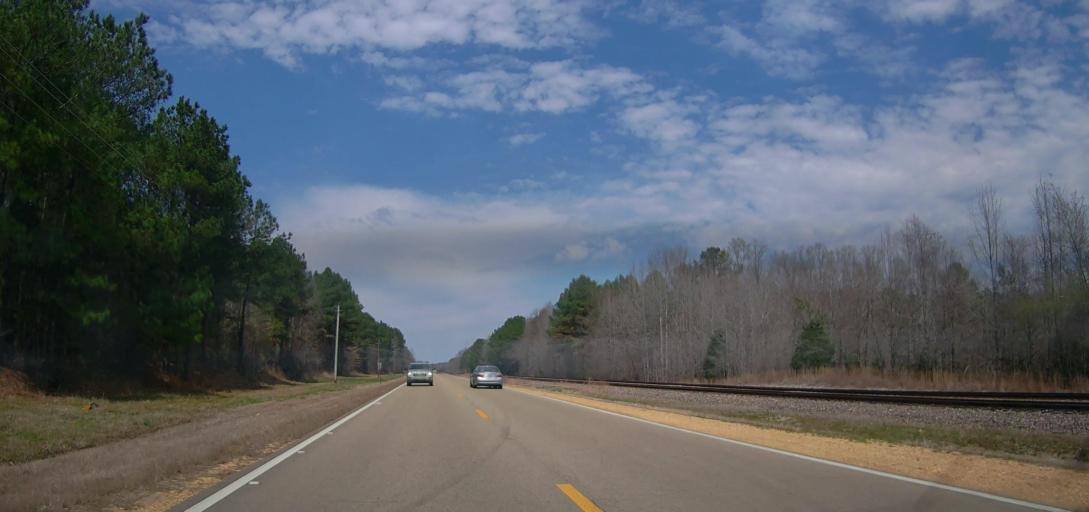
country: US
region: Mississippi
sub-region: Union County
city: New Albany
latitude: 34.5836
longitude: -89.1323
